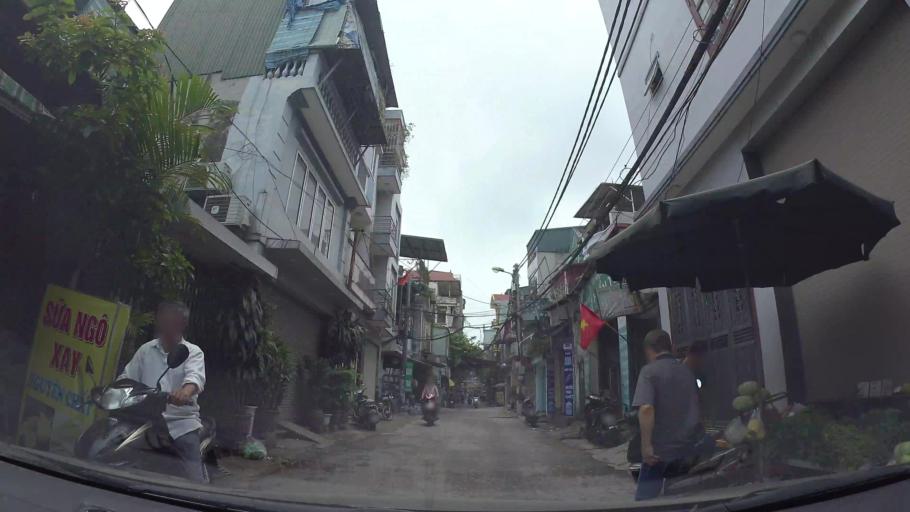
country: VN
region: Ha Noi
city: Hai BaTrung
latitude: 20.9799
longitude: 105.8481
